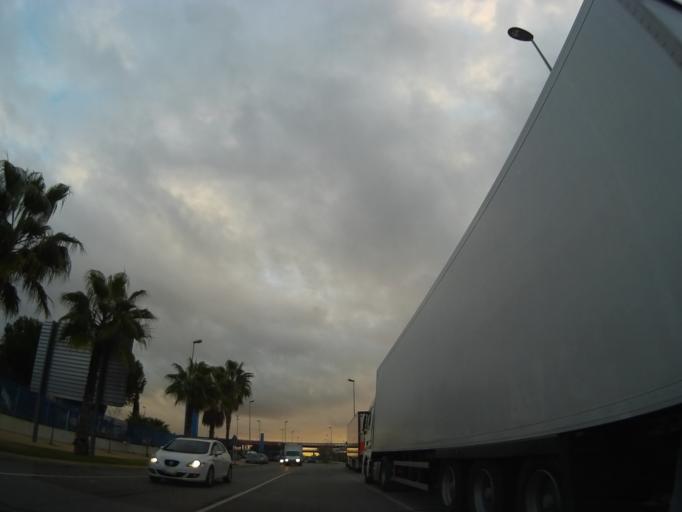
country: ES
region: Andalusia
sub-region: Provincia de Malaga
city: Alhaurin de la Torre
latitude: 36.7125
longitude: -4.5134
